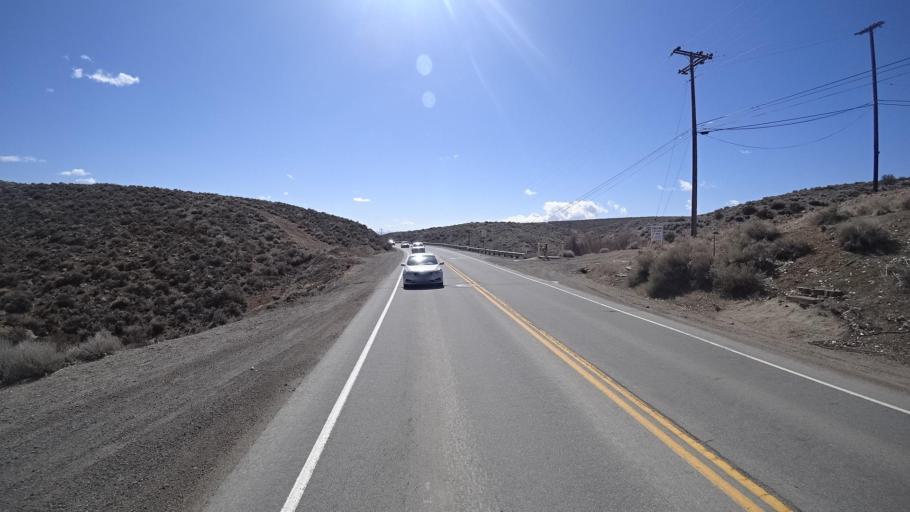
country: US
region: Nevada
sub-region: Washoe County
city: Golden Valley
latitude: 39.5891
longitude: -119.8349
